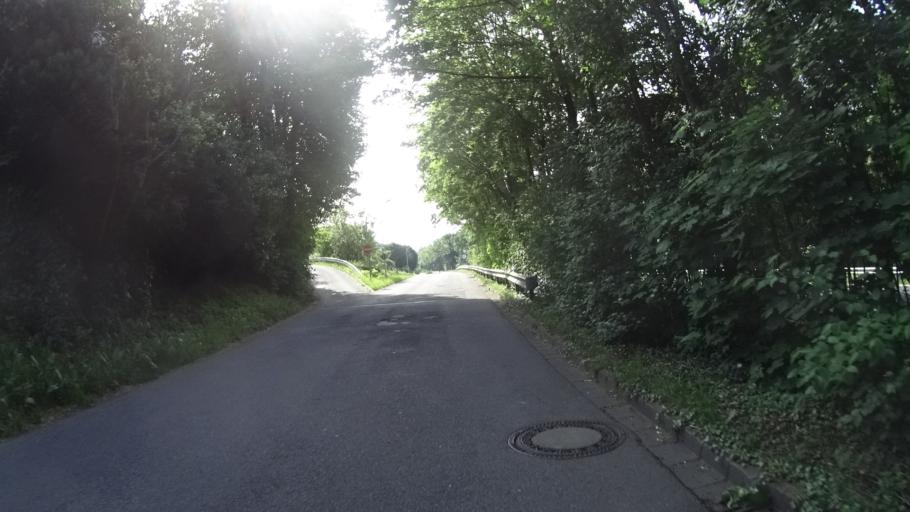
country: DE
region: Bavaria
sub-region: Lower Bavaria
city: Ihrlerstein
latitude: 48.9255
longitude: 11.8562
